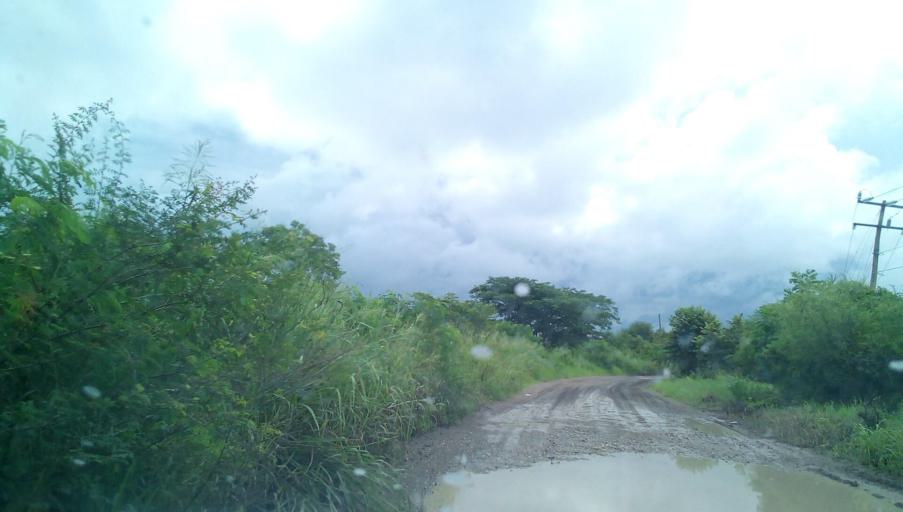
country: MX
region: Veracruz
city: Panuco
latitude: 21.8500
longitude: -98.1425
